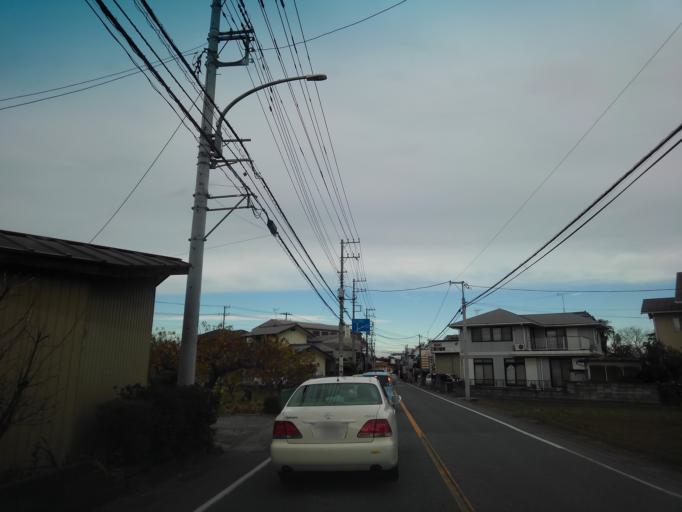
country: JP
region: Saitama
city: Morohongo
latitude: 35.9095
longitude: 139.3330
